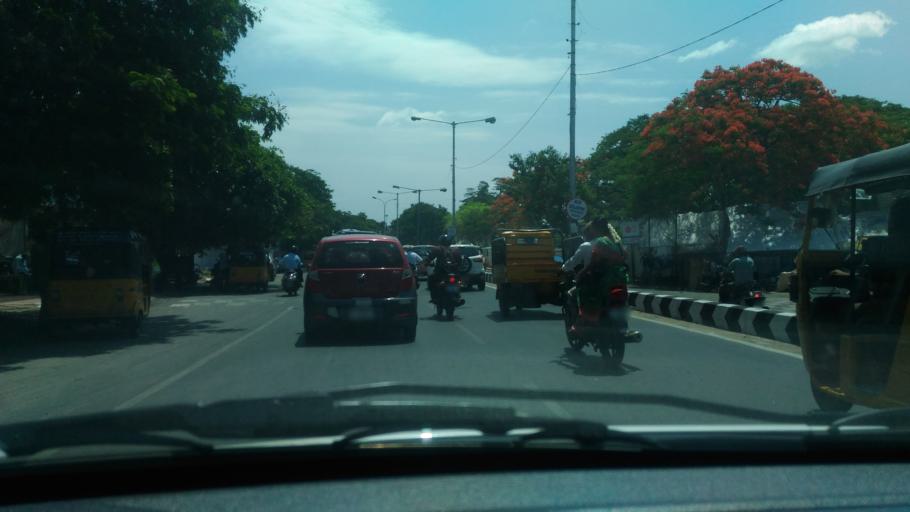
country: IN
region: Tamil Nadu
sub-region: Chennai
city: Chetput
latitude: 13.0483
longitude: 80.2459
